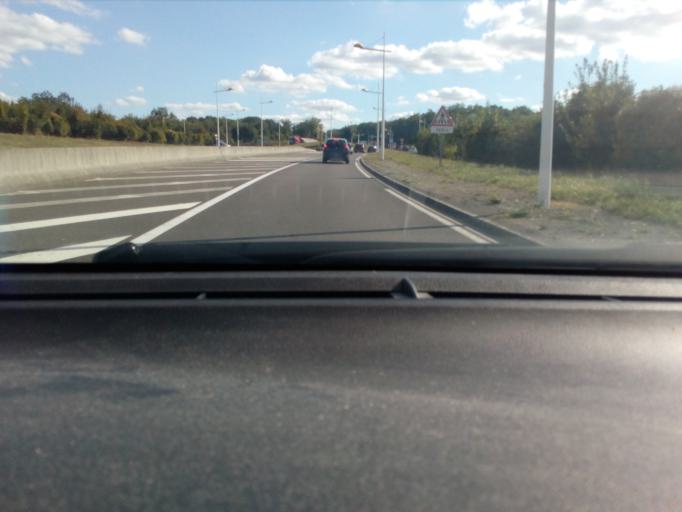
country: FR
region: Poitou-Charentes
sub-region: Departement de la Charente
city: Soyaux
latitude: 45.6523
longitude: 0.2089
